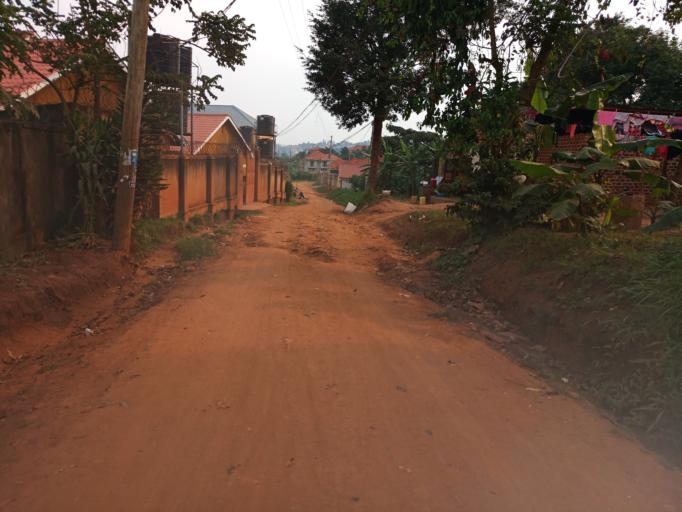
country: UG
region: Central Region
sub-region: Wakiso District
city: Kireka
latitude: 0.3904
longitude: 32.6388
